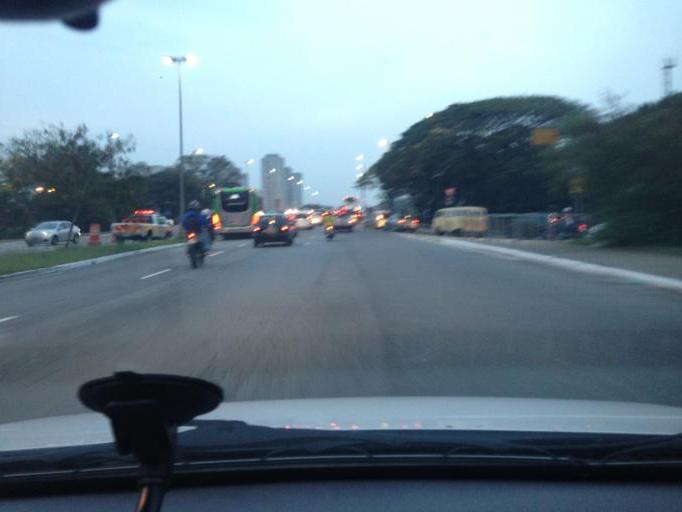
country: BR
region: Sao Paulo
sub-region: Sao Paulo
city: Sao Paulo
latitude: -23.5109
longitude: -46.7054
